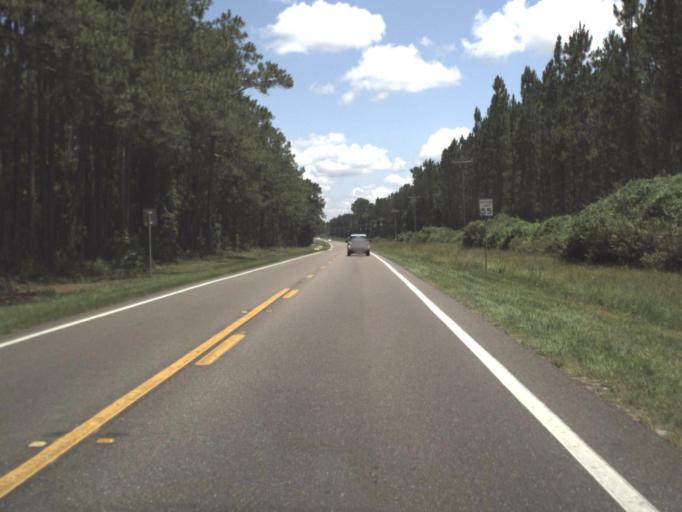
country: US
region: Florida
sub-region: Clay County
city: Keystone Heights
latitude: 29.7335
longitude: -82.0489
